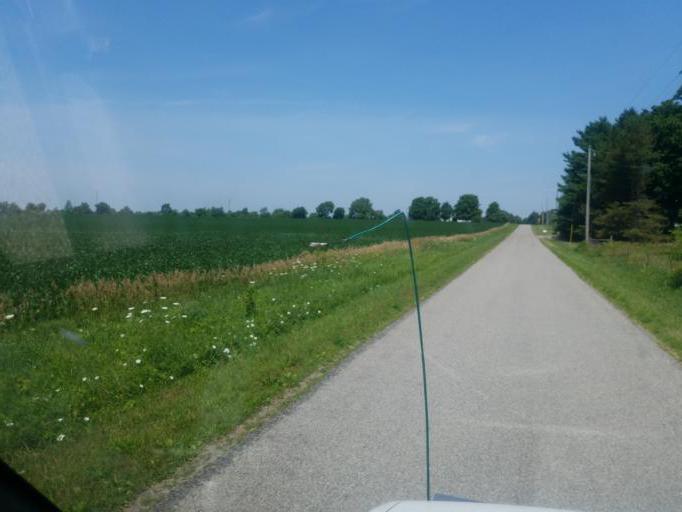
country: US
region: Ohio
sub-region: Logan County
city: West Liberty
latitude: 40.2823
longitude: -83.7689
